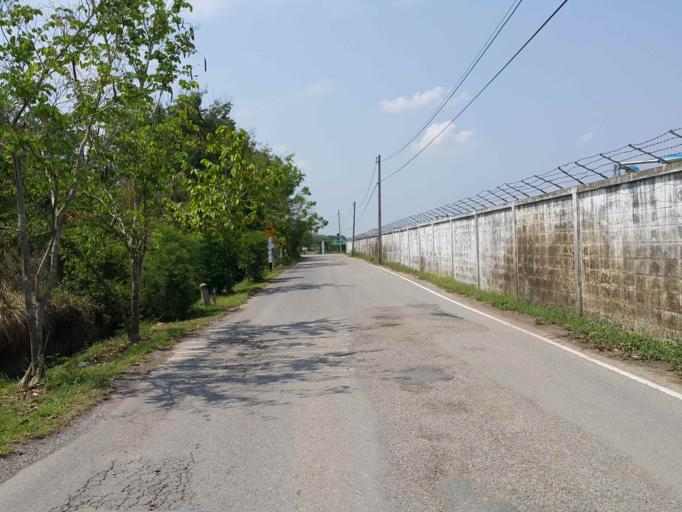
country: TH
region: Chiang Mai
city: Chiang Mai
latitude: 18.7575
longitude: 98.9607
